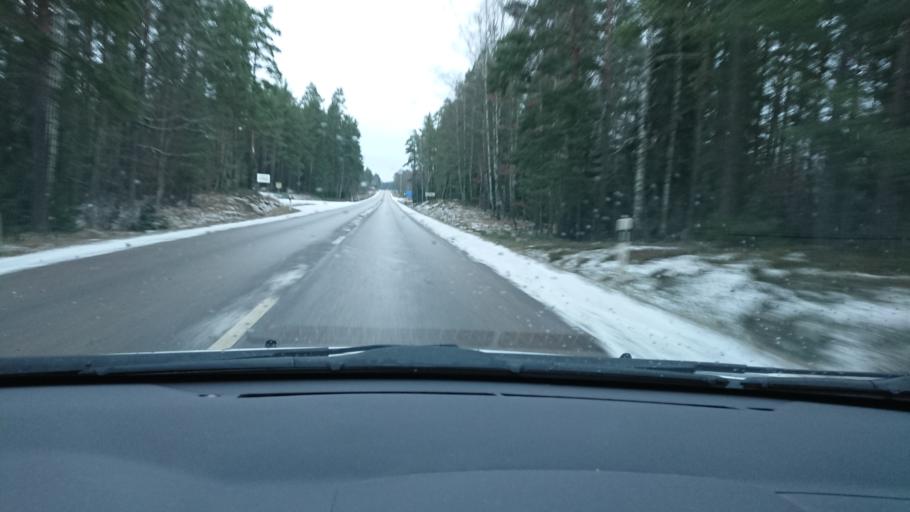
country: SE
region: Kalmar
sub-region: Hultsfreds Kommun
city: Hultsfred
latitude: 57.5308
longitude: 15.8439
